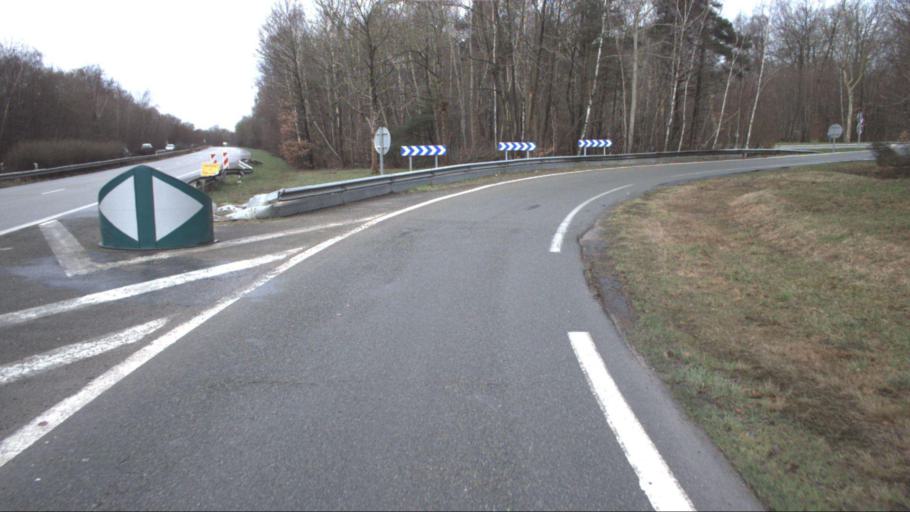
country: FR
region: Ile-de-France
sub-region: Departement des Yvelines
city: La Queue-les-Yvelines
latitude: 48.7996
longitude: 1.7425
